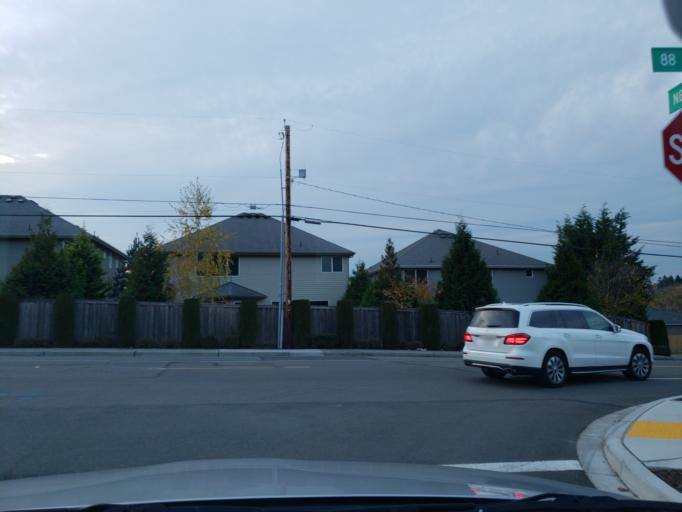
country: US
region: Washington
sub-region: King County
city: Bothell
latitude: 47.7746
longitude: -122.2230
